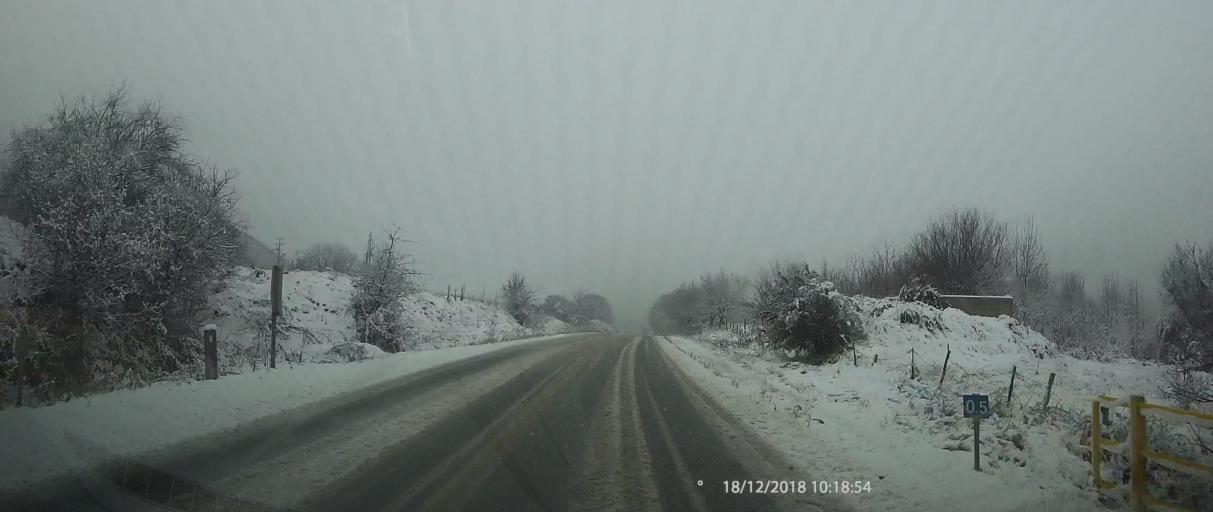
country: GR
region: Thessaly
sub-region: Nomos Larisis
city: Livadi
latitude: 40.1353
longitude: 22.2197
